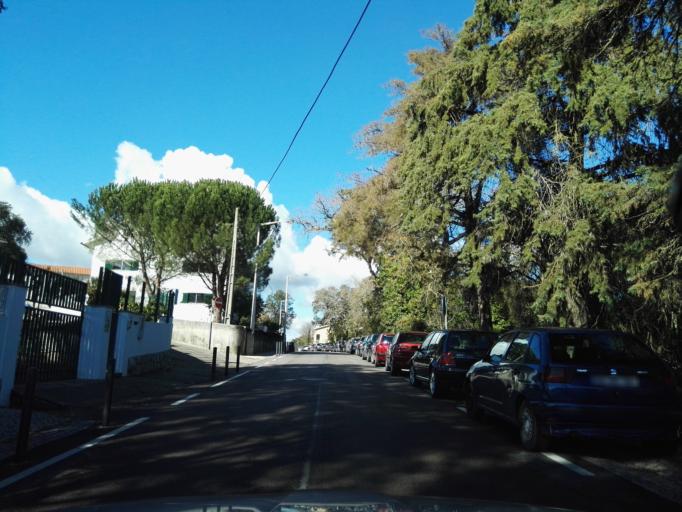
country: PT
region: Santarem
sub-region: Ourem
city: Fatima
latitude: 39.6332
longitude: -8.6773
